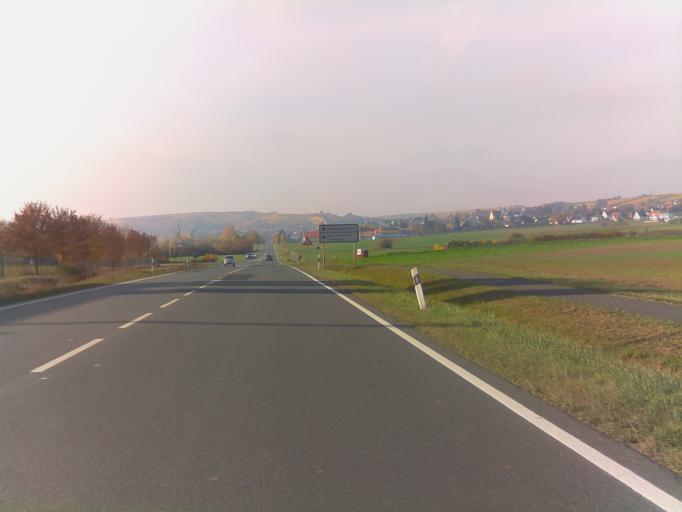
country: DE
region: Bavaria
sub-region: Regierungsbezirk Unterfranken
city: Dettelbach
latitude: 49.8032
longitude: 10.1940
